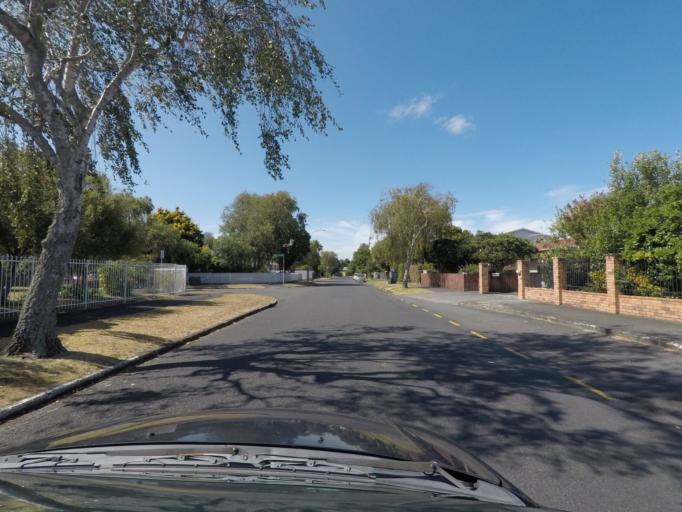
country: NZ
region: Auckland
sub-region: Auckland
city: Rosebank
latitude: -36.8871
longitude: 174.6779
